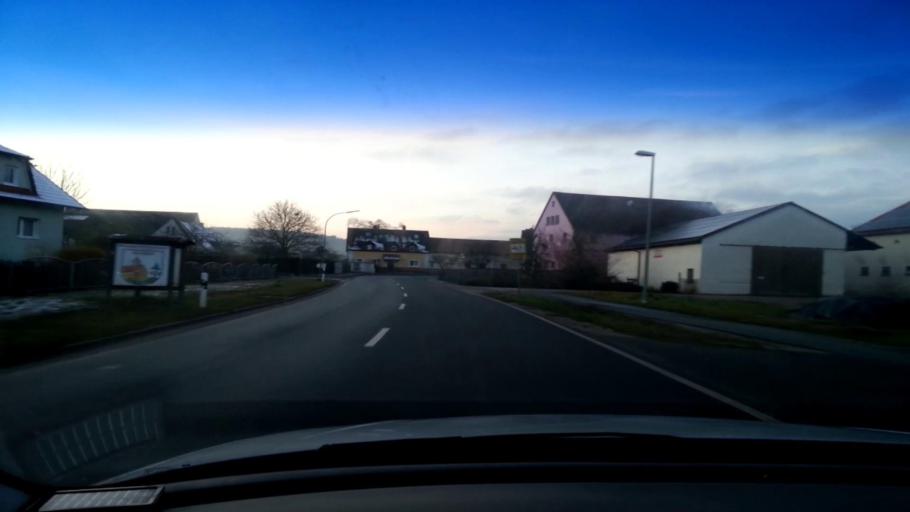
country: DE
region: Bavaria
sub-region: Upper Franconia
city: Pommersfelden
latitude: 49.7843
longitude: 10.8231
